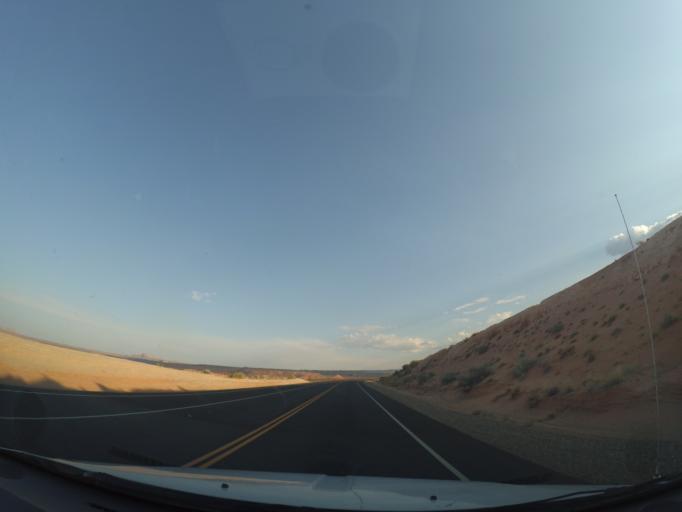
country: US
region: Arizona
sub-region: Coconino County
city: Page
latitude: 36.9700
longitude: -111.4901
